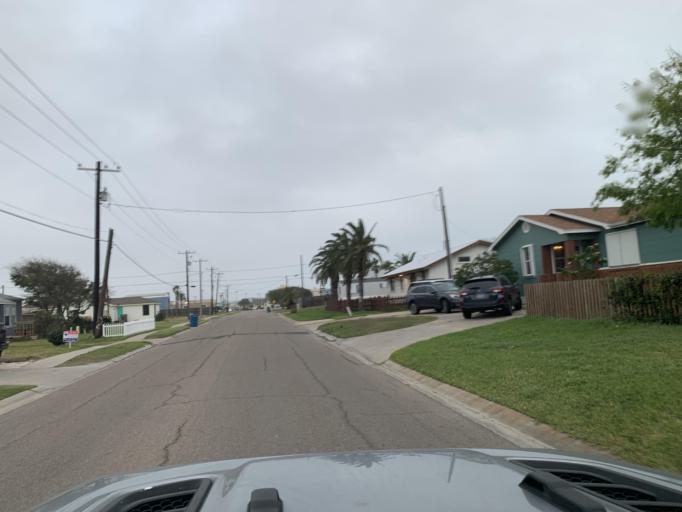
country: US
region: Texas
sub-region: Nueces County
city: Port Aransas
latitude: 27.8295
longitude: -97.0619
